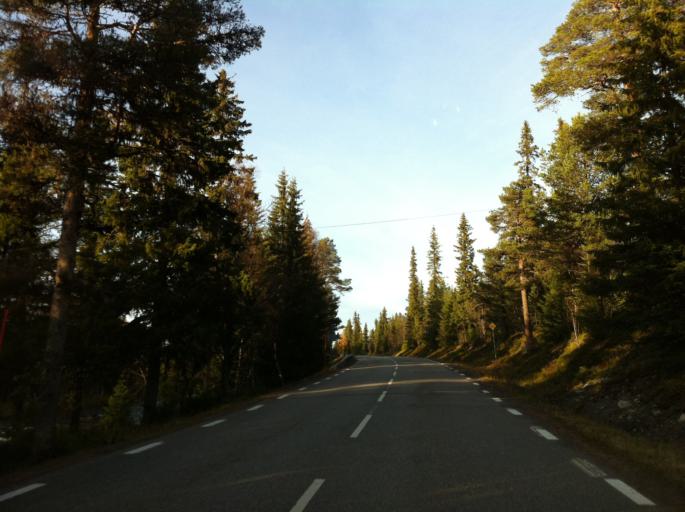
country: NO
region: Hedmark
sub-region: Engerdal
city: Engerdal
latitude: 62.0691
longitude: 12.3138
